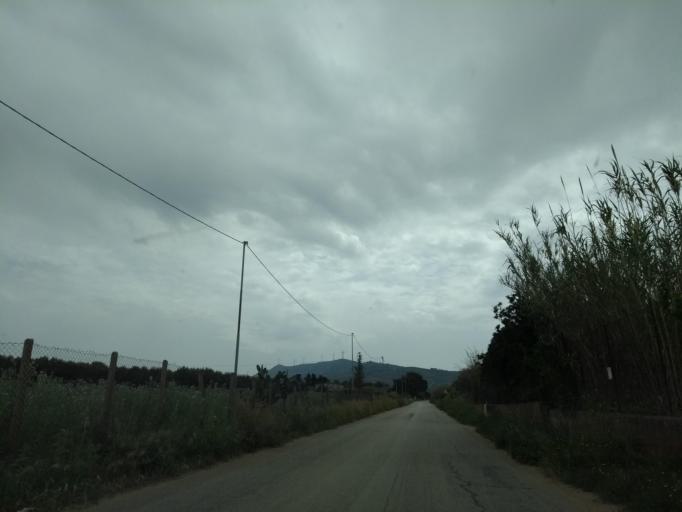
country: IT
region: Sicily
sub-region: Palermo
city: Partinico
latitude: 37.9982
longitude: 13.0650
